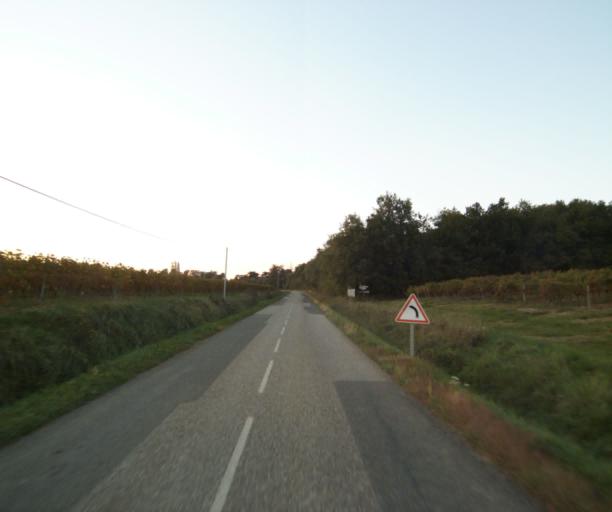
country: FR
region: Midi-Pyrenees
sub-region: Departement du Gers
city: Vic-Fezensac
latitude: 43.7995
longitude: 0.2357
